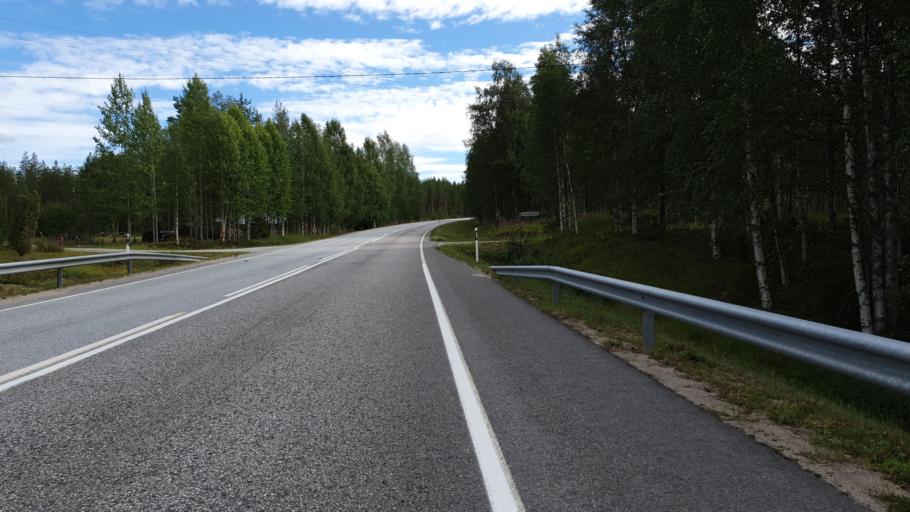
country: FI
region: Kainuu
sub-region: Kehys-Kainuu
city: Kuhmo
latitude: 64.4888
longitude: 29.8120
